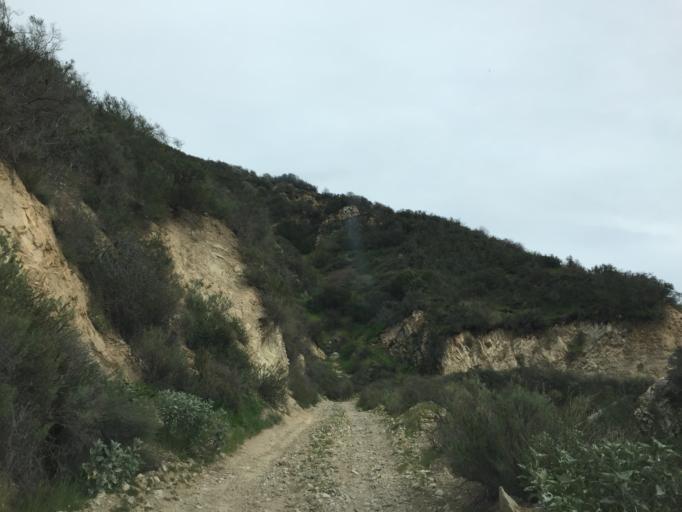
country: US
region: California
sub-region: San Bernardino County
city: Running Springs
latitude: 34.1309
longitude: -117.0722
